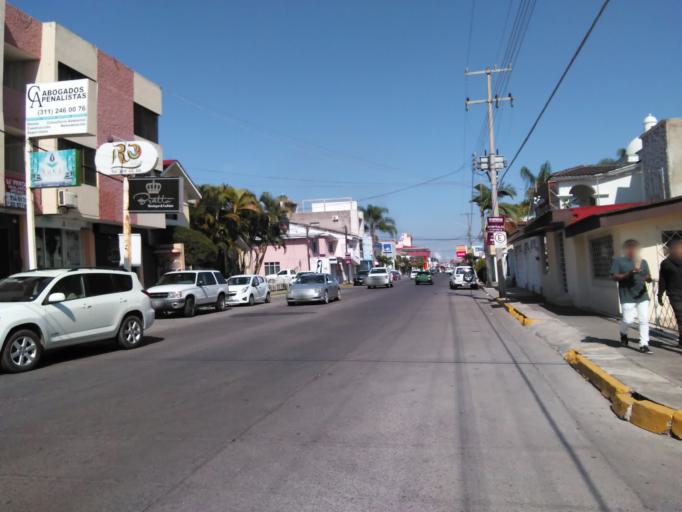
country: MX
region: Nayarit
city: Tepic
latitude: 21.4879
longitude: -104.8855
